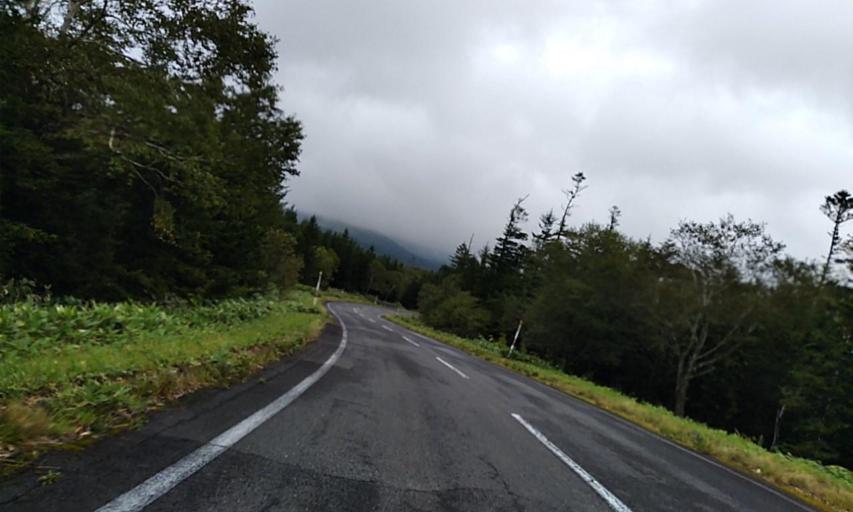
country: JP
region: Hokkaido
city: Abashiri
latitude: 43.6060
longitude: 144.5870
